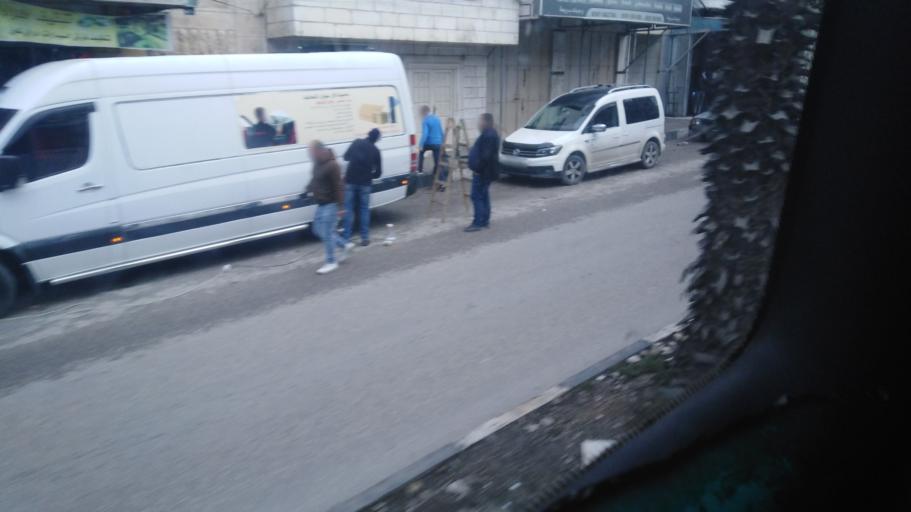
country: PS
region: West Bank
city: Hebron
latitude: 31.5310
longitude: 35.0901
